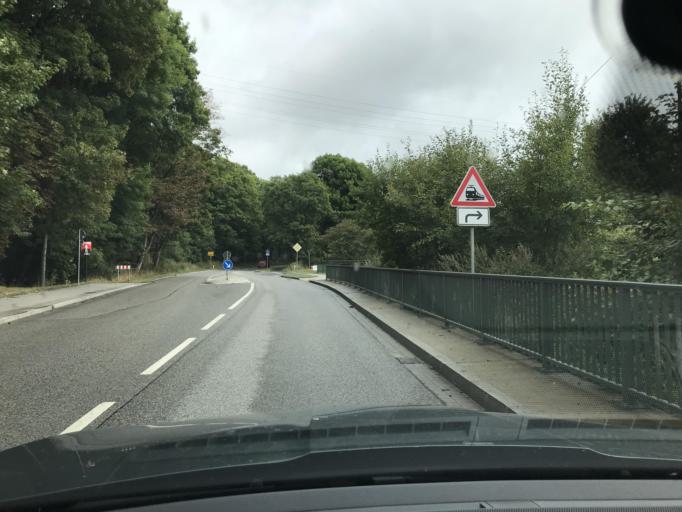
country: DE
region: Saxony-Anhalt
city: Elbingerode
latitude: 51.7688
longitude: 10.8119
